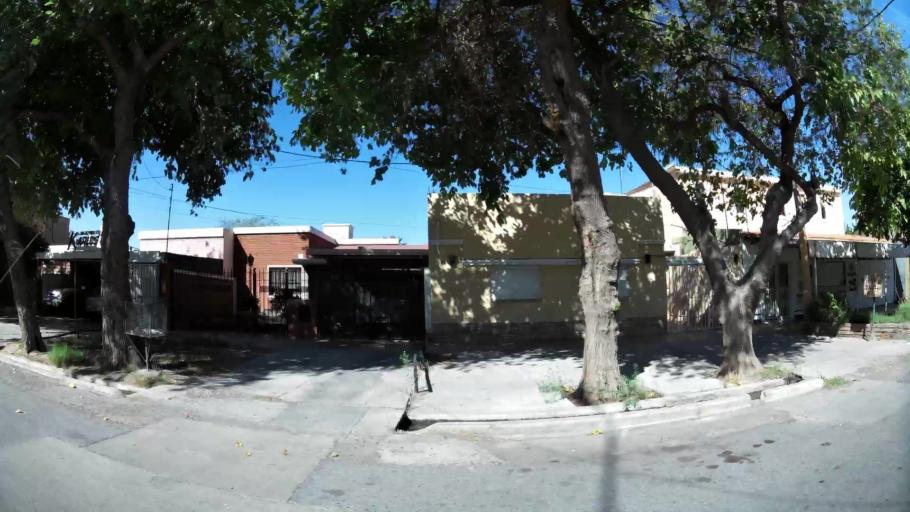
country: AR
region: San Juan
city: San Juan
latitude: -31.5252
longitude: -68.5363
